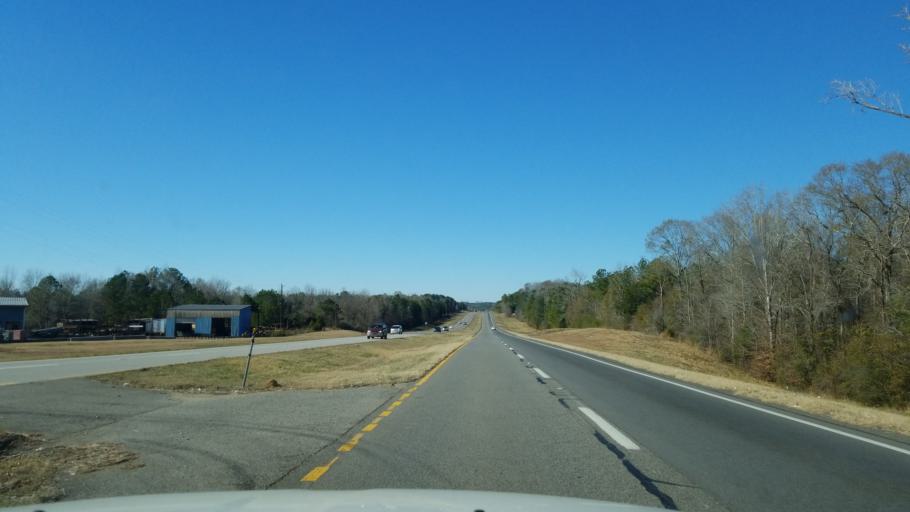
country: US
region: Alabama
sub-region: Tuscaloosa County
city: Northport
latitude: 33.2526
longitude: -87.6876
